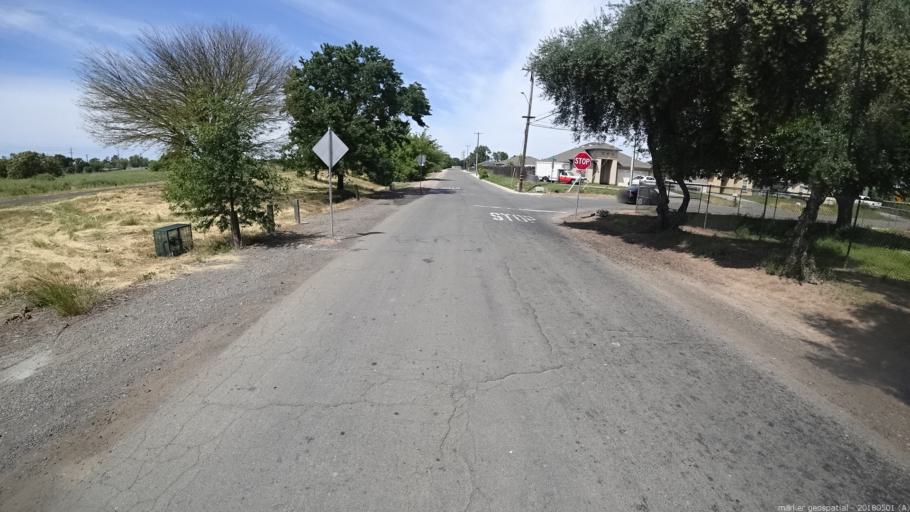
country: US
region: California
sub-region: Sacramento County
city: Rio Linda
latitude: 38.6636
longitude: -121.4472
